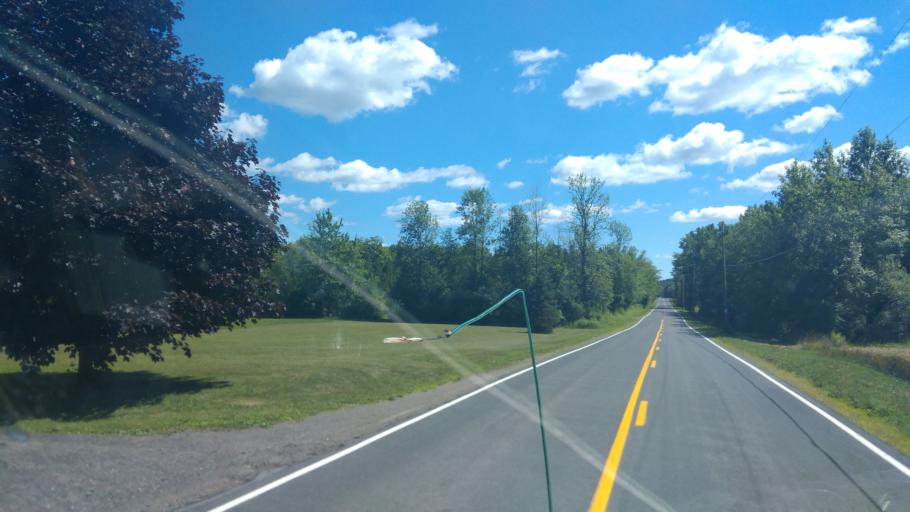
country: US
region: New York
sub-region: Wayne County
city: Sodus
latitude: 43.1870
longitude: -77.0503
